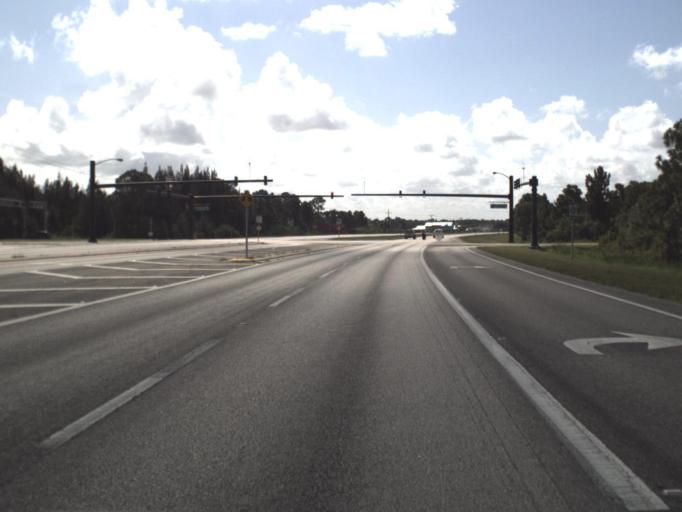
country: US
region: Florida
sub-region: Charlotte County
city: Charlotte Park
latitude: 26.8589
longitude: -81.9890
